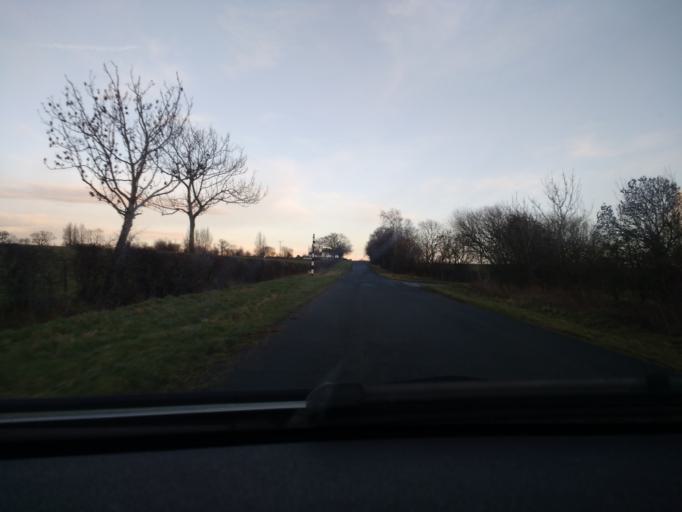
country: GB
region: England
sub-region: Cumbria
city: Carlisle
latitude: 54.7308
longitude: -2.9666
